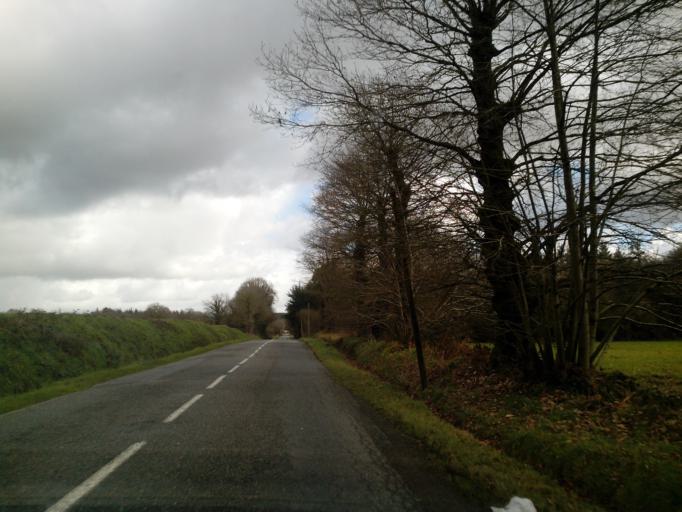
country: FR
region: Brittany
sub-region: Departement des Cotes-d'Armor
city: Broons
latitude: 48.2811
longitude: -2.3051
